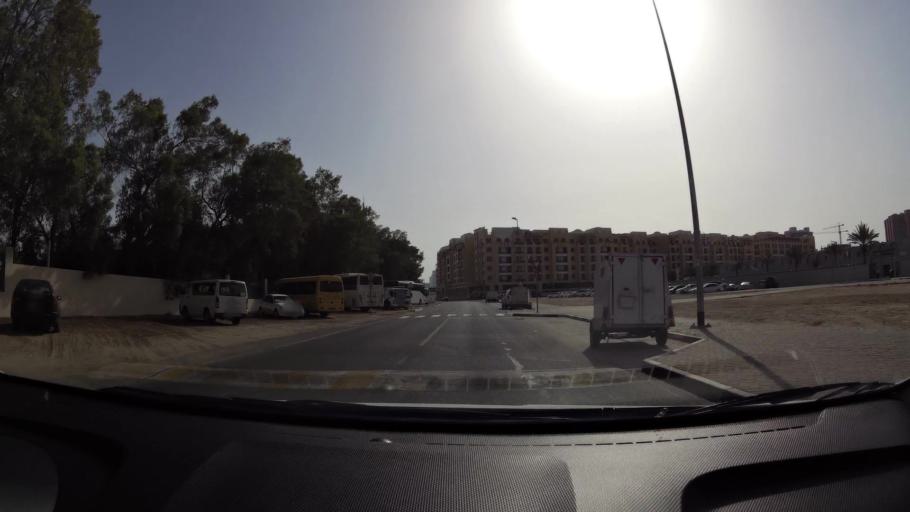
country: AE
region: Ash Shariqah
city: Sharjah
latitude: 25.2901
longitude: 55.3509
